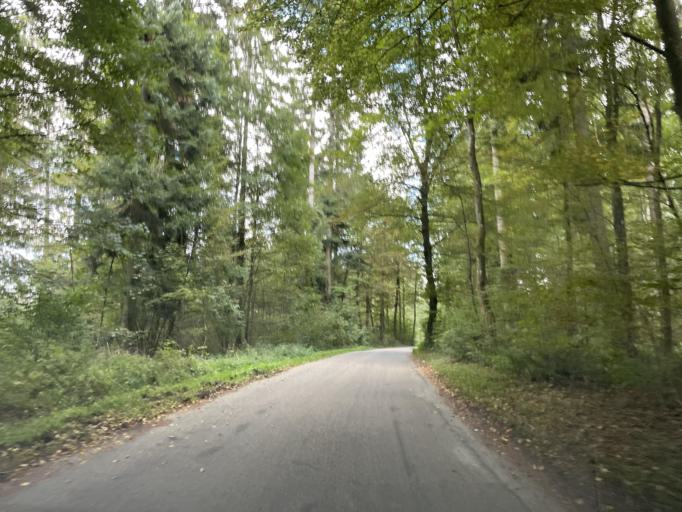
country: CH
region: Zurich
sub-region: Bezirk Winterthur
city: Seen (Kreis 3) / Ganzenbuehl
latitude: 47.4740
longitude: 8.7587
